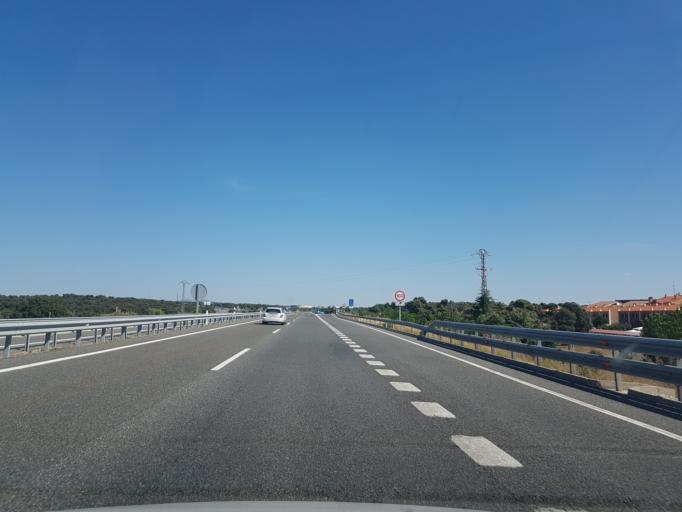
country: ES
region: Castille and Leon
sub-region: Provincia de Avila
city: Avila
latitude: 40.6708
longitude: -4.6564
